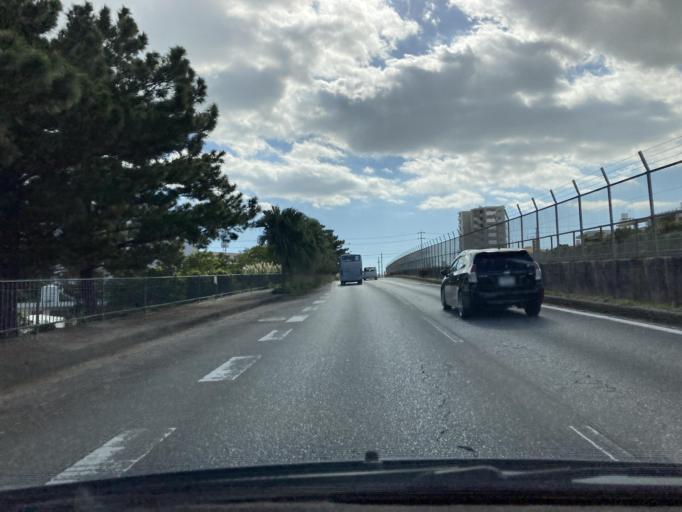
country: JP
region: Okinawa
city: Okinawa
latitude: 26.3281
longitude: 127.7858
